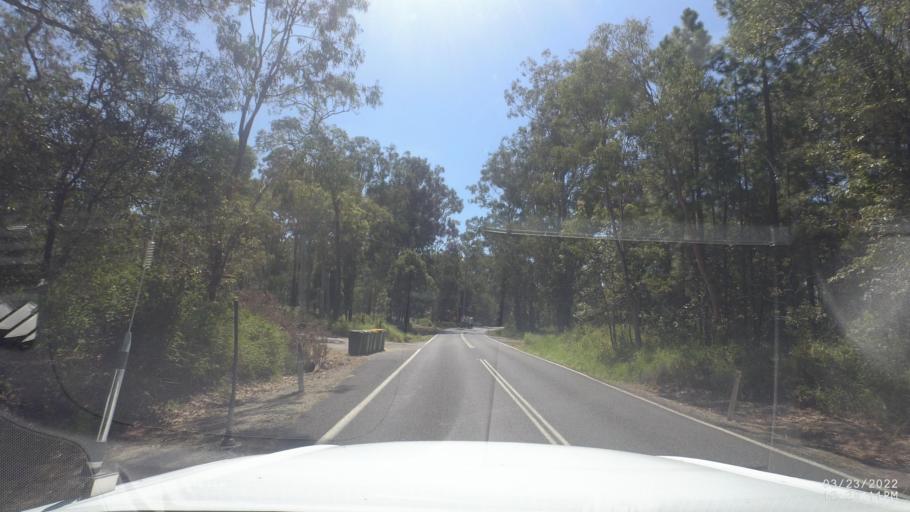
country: AU
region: Queensland
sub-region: Logan
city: Chambers Flat
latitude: -27.8074
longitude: 153.0974
